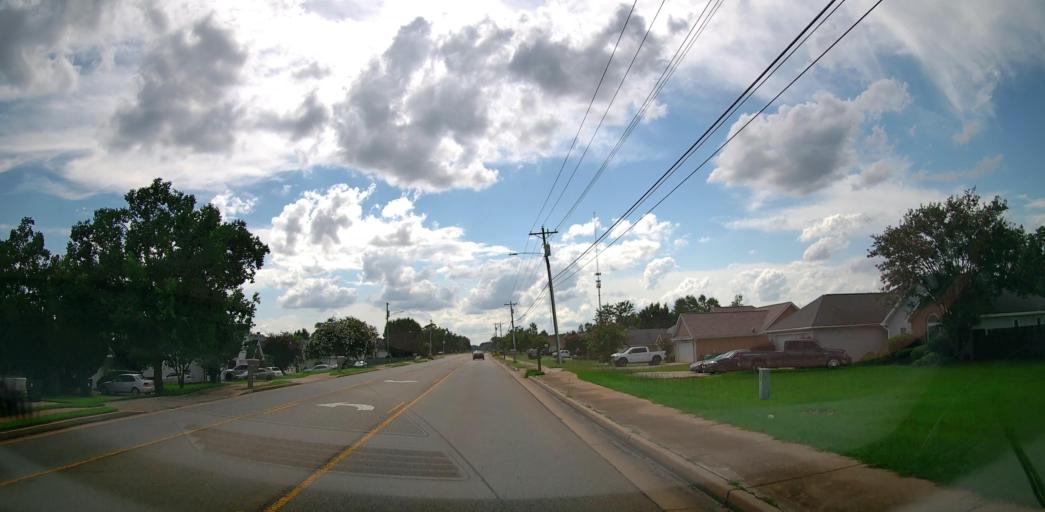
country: US
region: Georgia
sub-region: Houston County
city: Centerville
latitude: 32.5710
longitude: -83.6649
